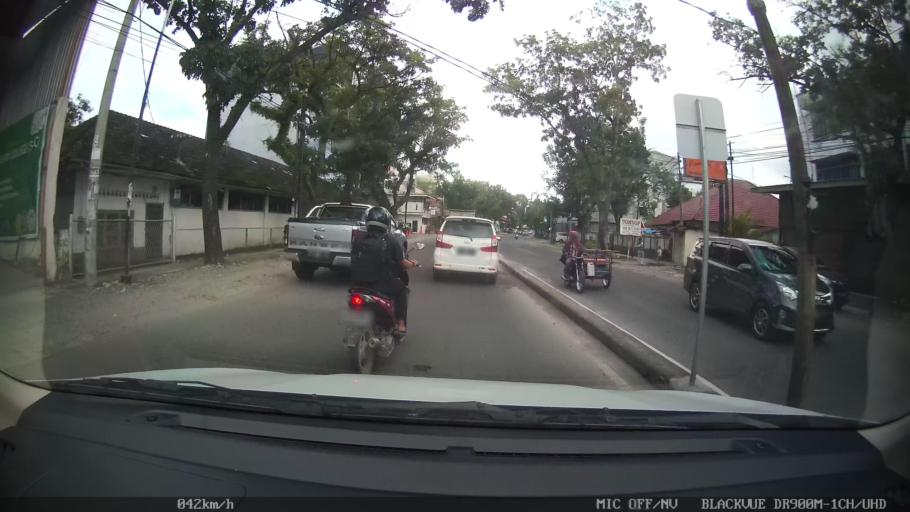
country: ID
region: North Sumatra
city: Medan
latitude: 3.6124
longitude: 98.6735
